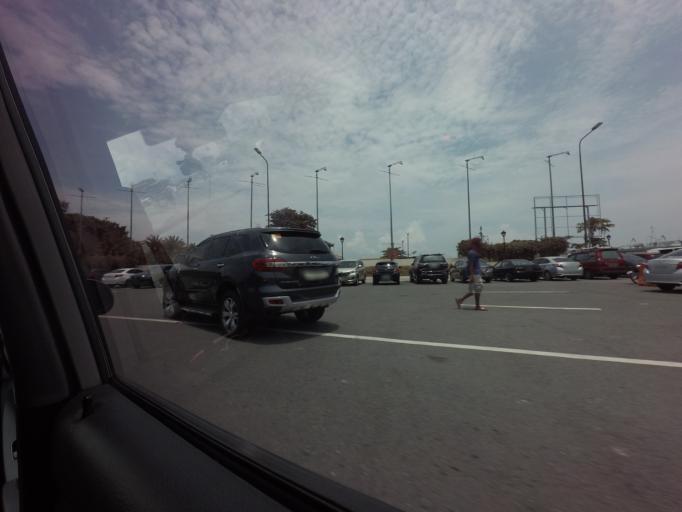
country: PH
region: Metro Manila
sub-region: City of Manila
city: Port Area
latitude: 14.5817
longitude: 120.9735
